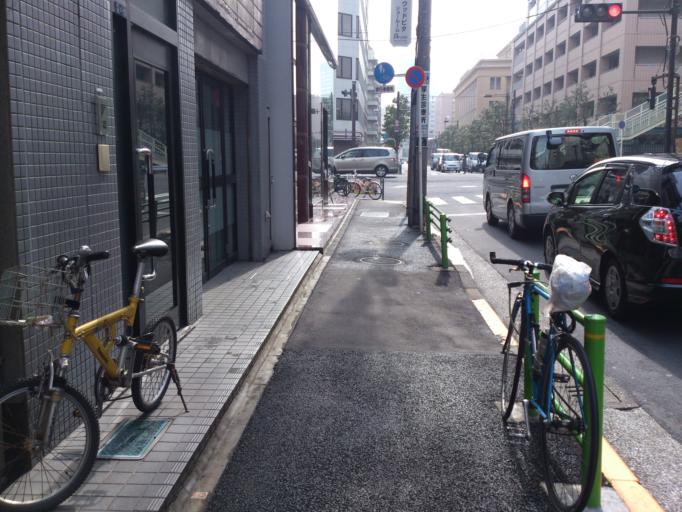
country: JP
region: Tokyo
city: Tokyo
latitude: 35.6703
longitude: 139.7776
